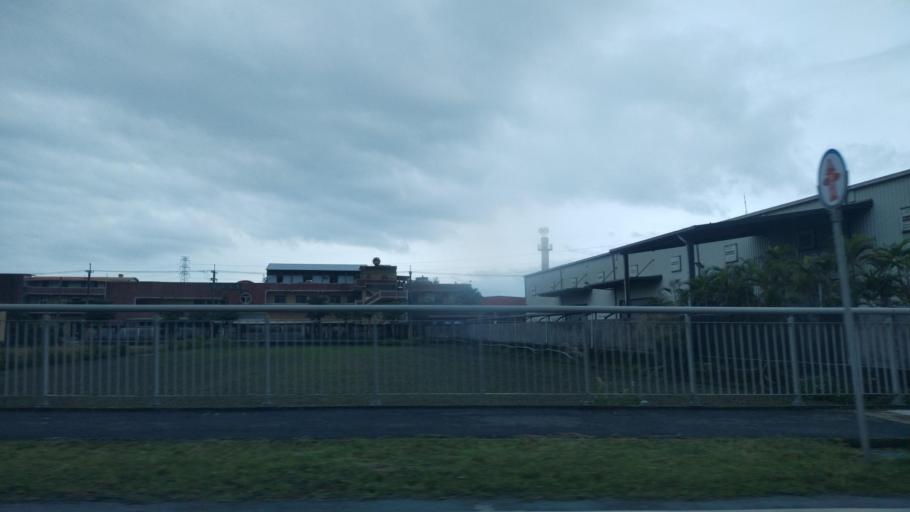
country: TW
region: Taiwan
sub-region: Yilan
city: Yilan
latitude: 24.6119
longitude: 121.8342
